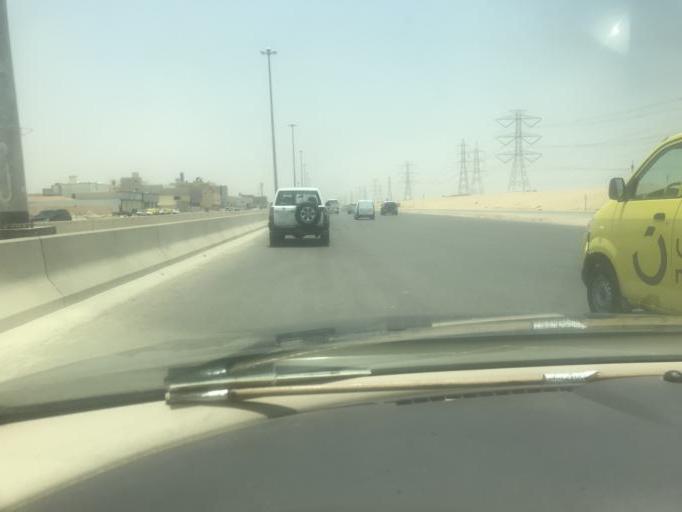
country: SA
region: Ar Riyad
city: Riyadh
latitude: 24.8189
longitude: 46.7374
